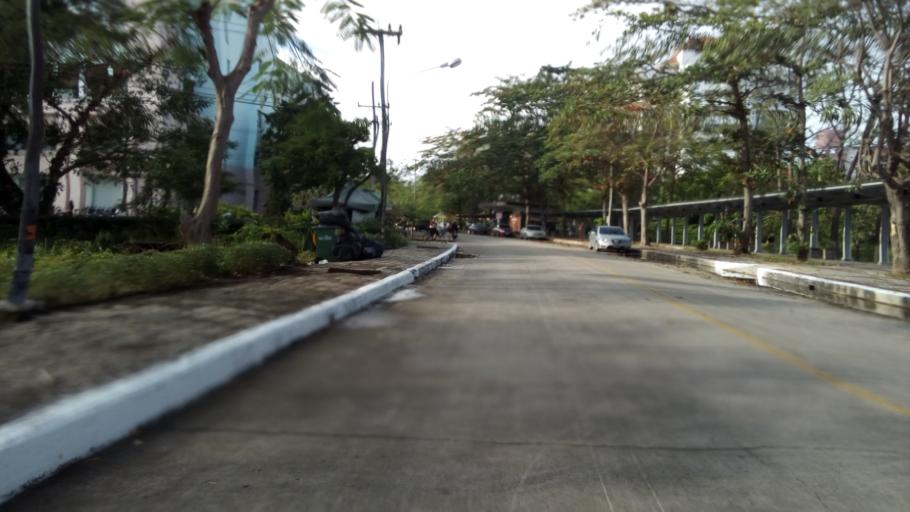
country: TH
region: Nakhon Nayok
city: Ongkharak
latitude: 14.1071
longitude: 100.9859
